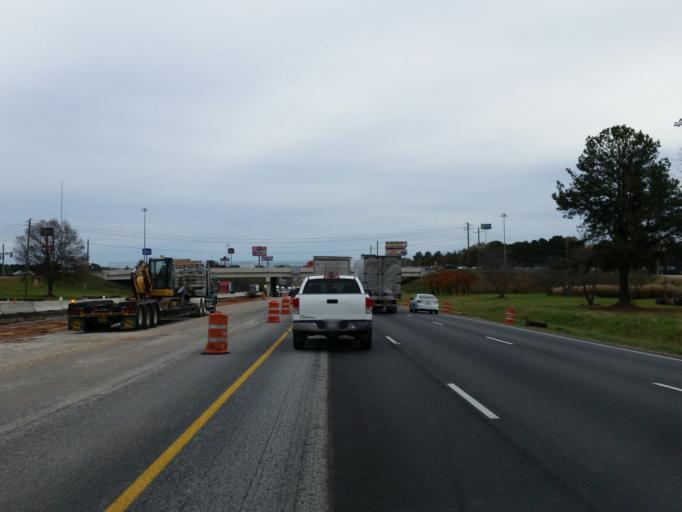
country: US
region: Georgia
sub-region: Henry County
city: McDonough
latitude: 33.4287
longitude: -84.1834
